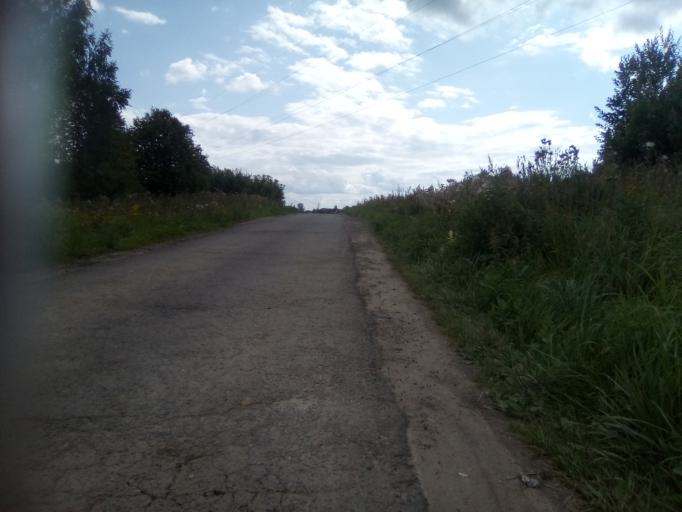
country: RU
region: Moskovskaya
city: Zhavoronki
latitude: 55.6626
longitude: 37.1359
